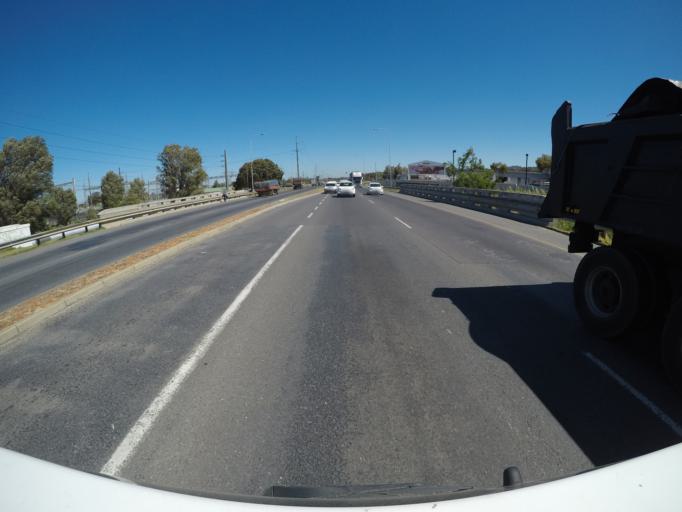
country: ZA
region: Western Cape
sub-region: Cape Winelands District Municipality
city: Stellenbosch
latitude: -34.0910
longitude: 18.8413
